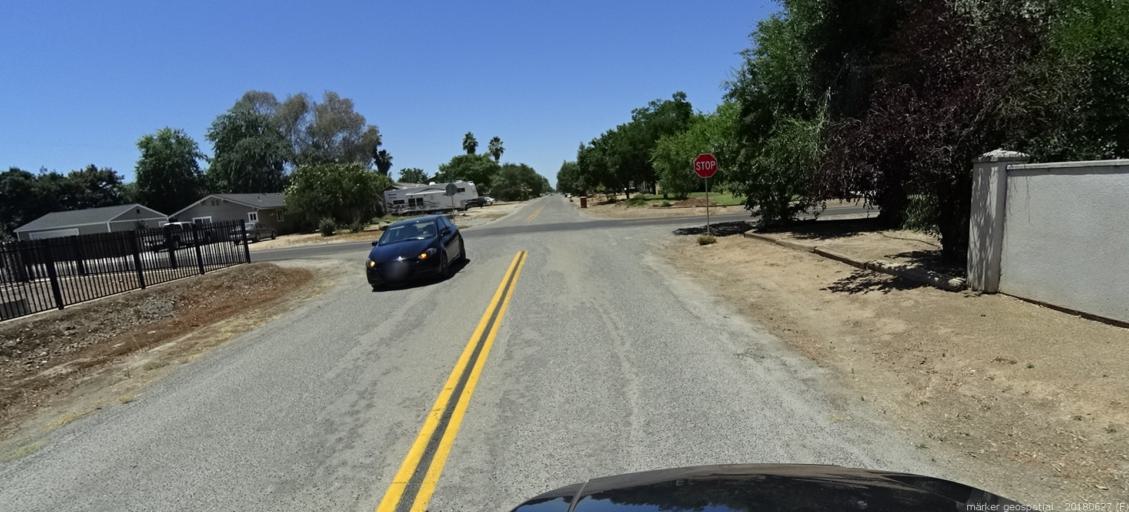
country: US
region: California
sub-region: Madera County
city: Bonadelle Ranchos-Madera Ranchos
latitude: 36.9240
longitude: -119.8777
